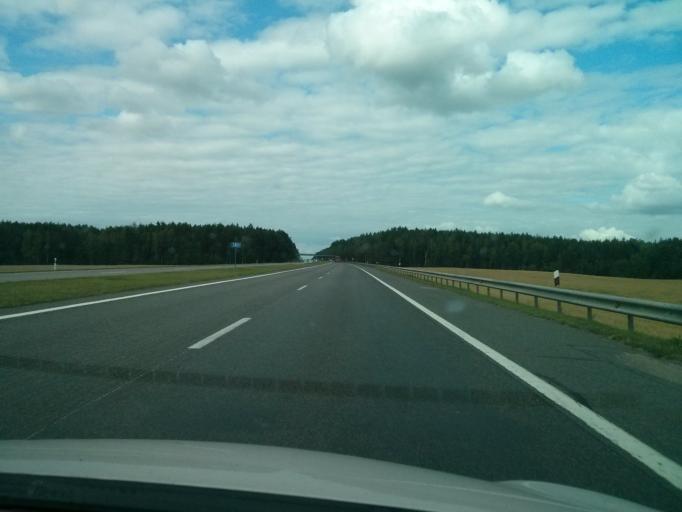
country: BY
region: Minsk
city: Zamostochcha
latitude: 53.8862
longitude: 27.9388
